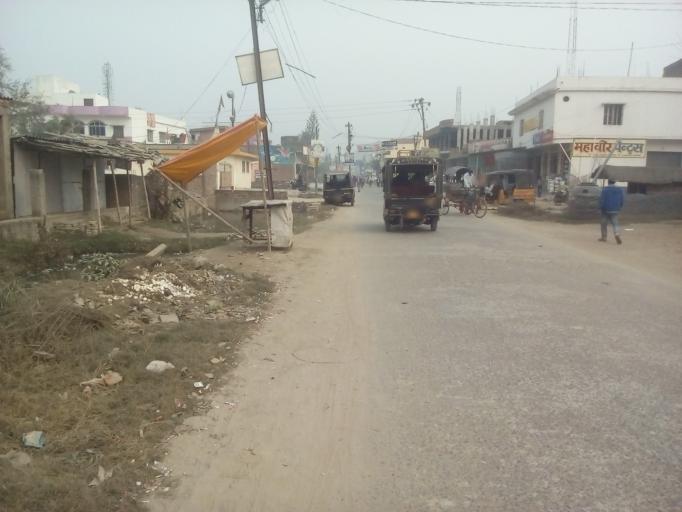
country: IN
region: Bihar
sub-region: Muzaffarpur
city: Muzaffarpur
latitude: 26.1031
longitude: 85.4014
